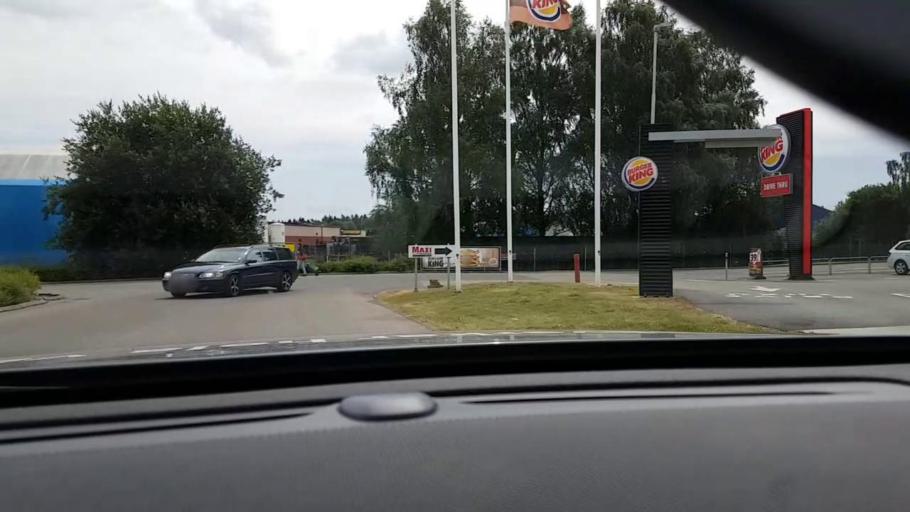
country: SE
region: Skane
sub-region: Hassleholms Kommun
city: Hassleholm
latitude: 56.1654
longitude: 13.7841
